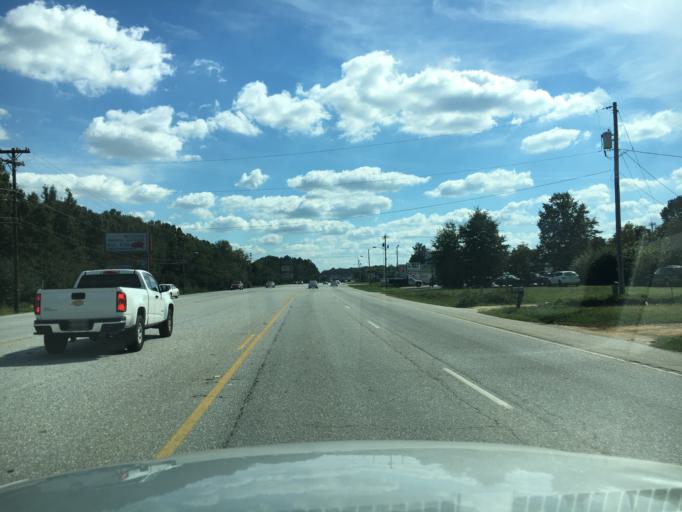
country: US
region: South Carolina
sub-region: Greenville County
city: Mauldin
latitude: 34.7943
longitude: -82.3143
